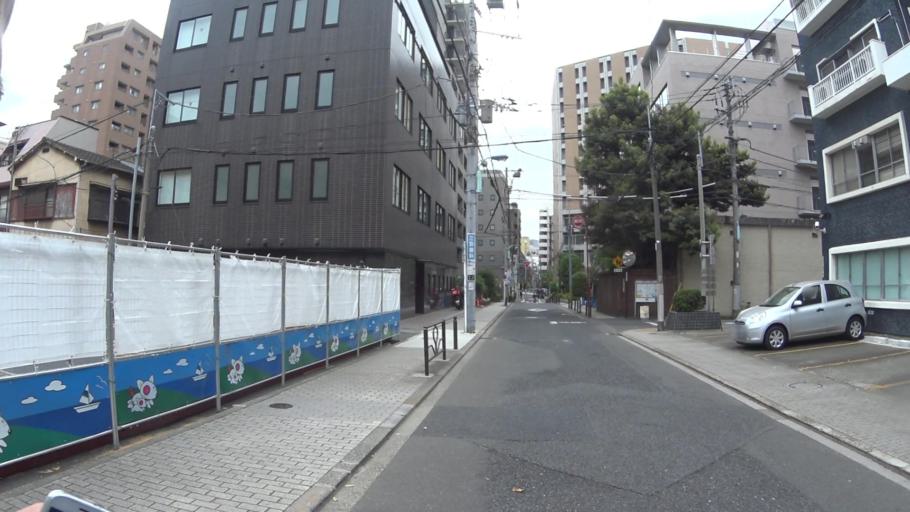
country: JP
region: Tokyo
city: Tokyo
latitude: 35.7058
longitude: 139.7576
